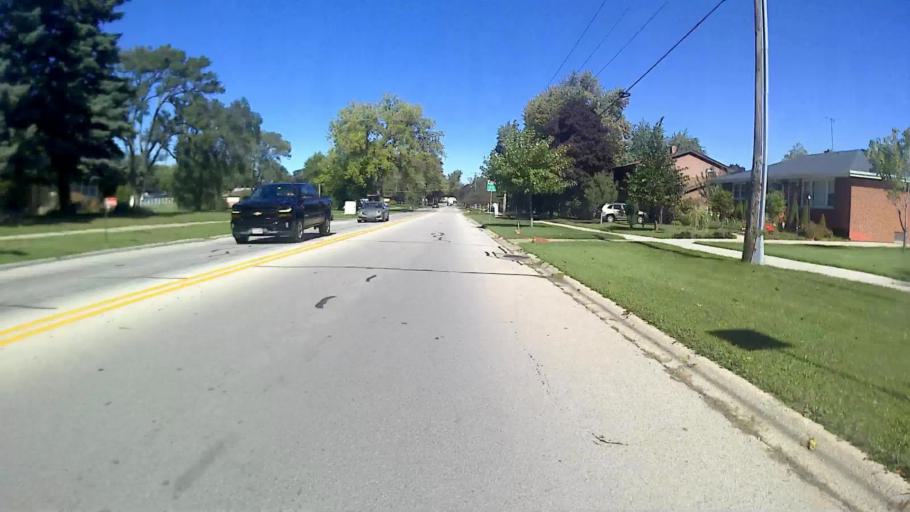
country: US
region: Illinois
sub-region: DuPage County
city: Addison
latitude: 41.9419
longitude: -88.0033
